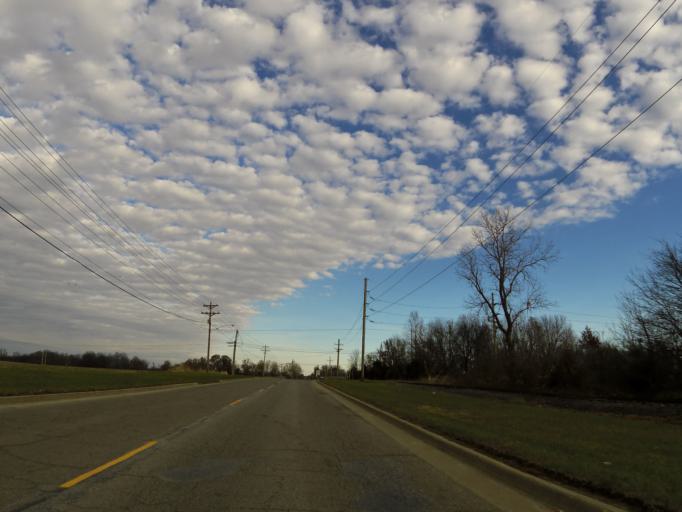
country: US
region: Illinois
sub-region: Jefferson County
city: Mount Vernon
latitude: 38.3302
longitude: -88.9700
